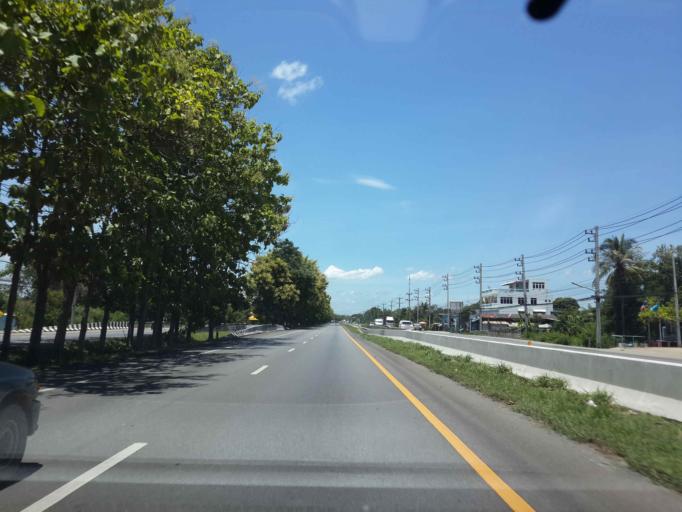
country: TH
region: Phetchaburi
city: Khao Yoi
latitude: 13.1974
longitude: 99.8307
